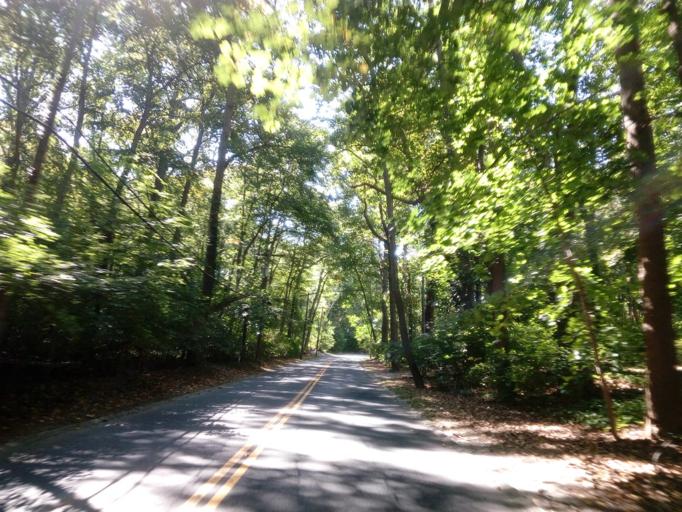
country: US
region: New York
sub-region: Nassau County
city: Oyster Bay Cove
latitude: 40.8586
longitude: -73.4957
